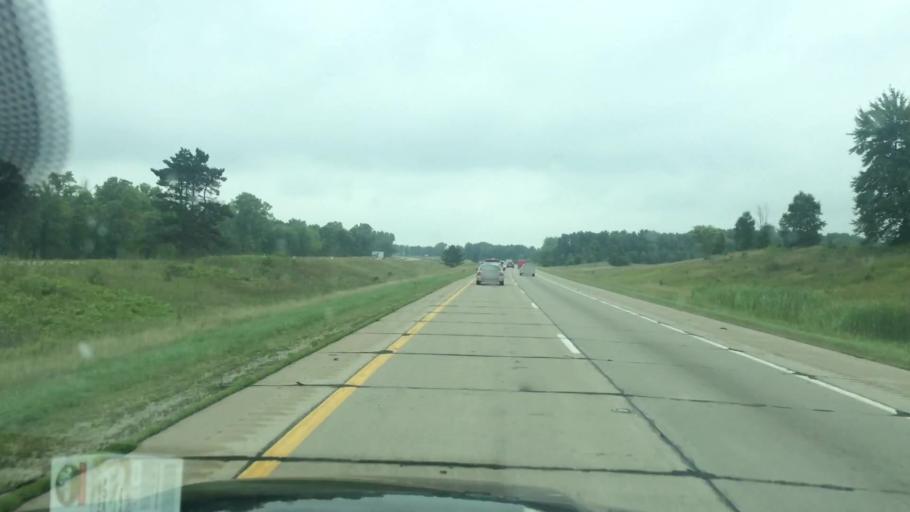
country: US
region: Michigan
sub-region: Eaton County
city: Olivet
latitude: 42.4873
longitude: -84.8720
